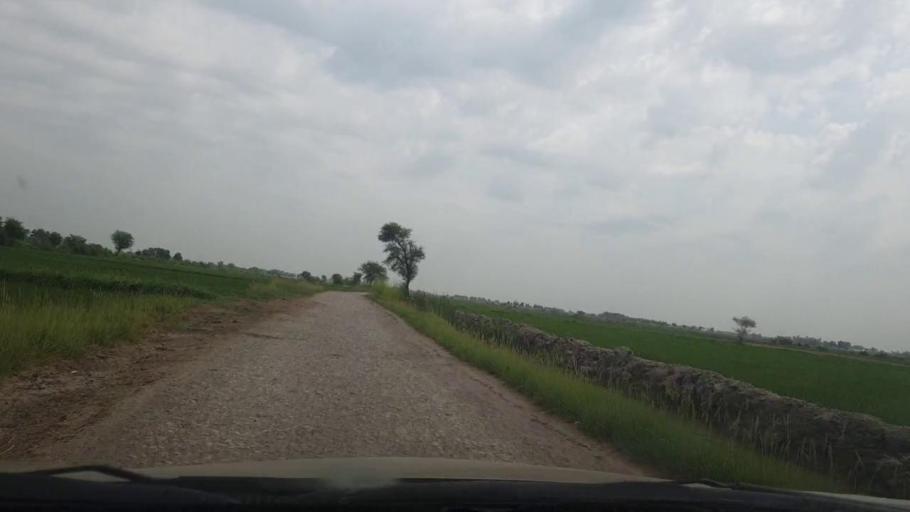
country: PK
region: Sindh
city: Ratodero
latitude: 27.7181
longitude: 68.2300
